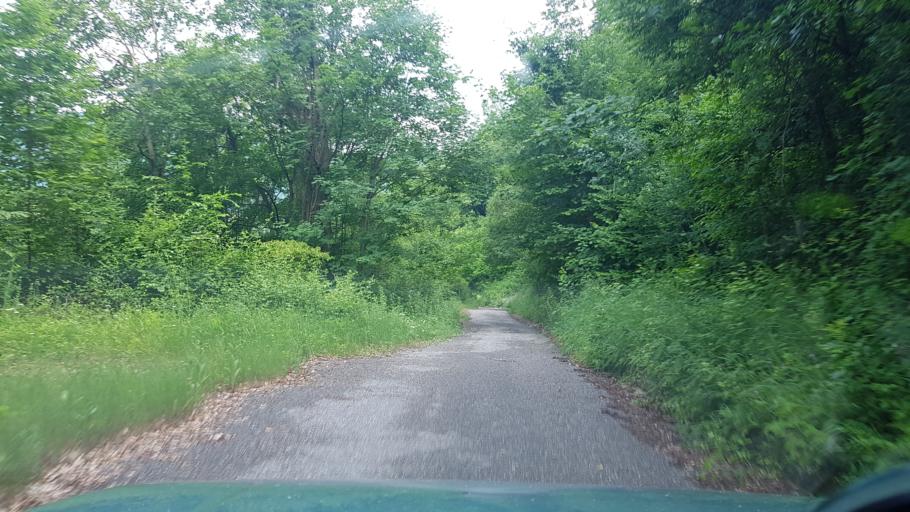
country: IT
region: Friuli Venezia Giulia
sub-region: Provincia di Udine
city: Torreano
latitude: 46.1630
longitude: 13.4418
